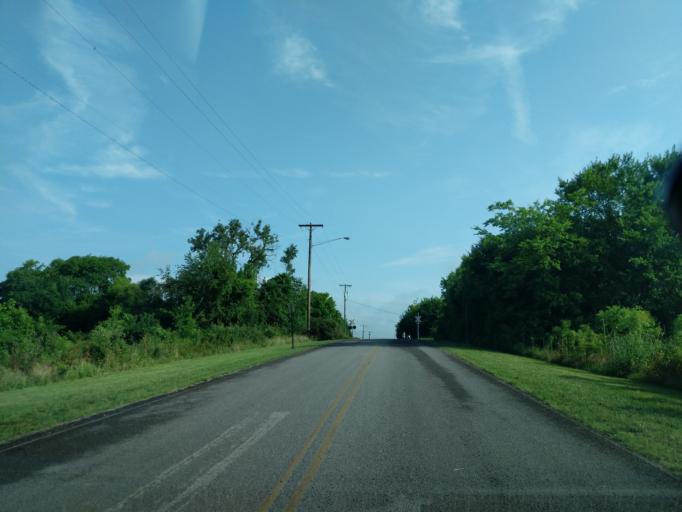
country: US
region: Tennessee
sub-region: Sumner County
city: Hendersonville
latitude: 36.3033
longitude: -86.6641
